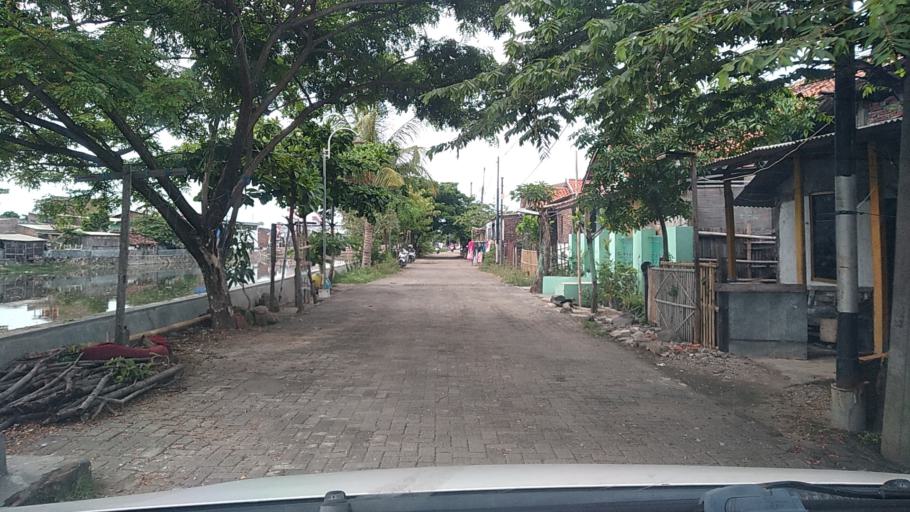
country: ID
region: Central Java
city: Semarang
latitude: -6.9576
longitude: 110.4404
